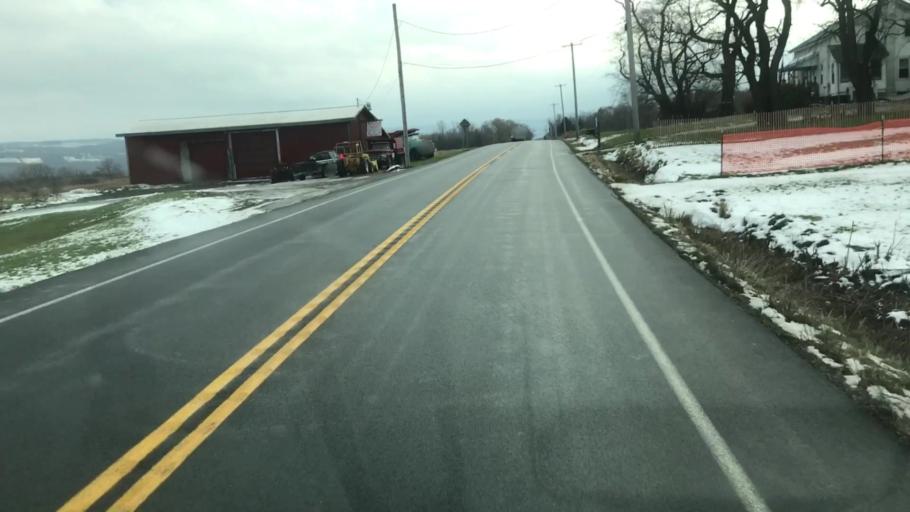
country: US
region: New York
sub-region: Onondaga County
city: Skaneateles
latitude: 42.8388
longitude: -76.3678
